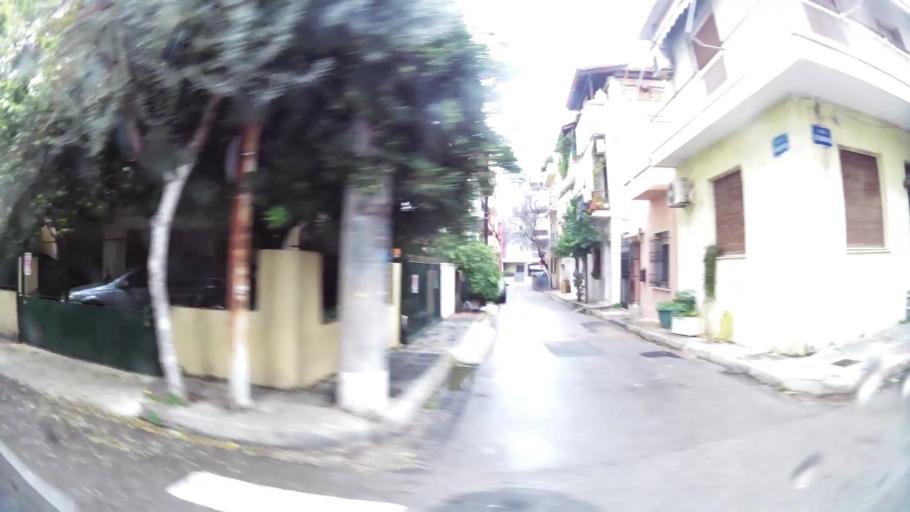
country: GR
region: Attica
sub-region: Nomarchia Athinas
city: Ymittos
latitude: 37.9566
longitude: 23.7514
